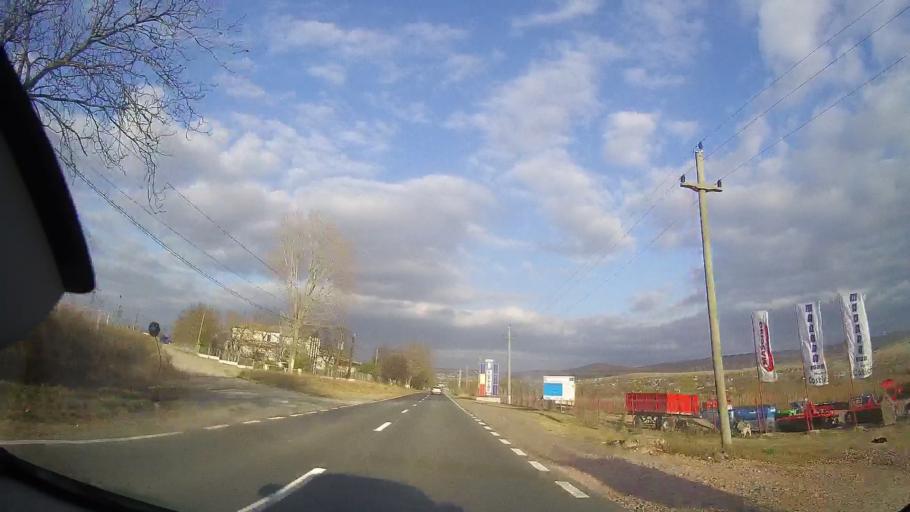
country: RO
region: Tulcea
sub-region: Comuna Topolog
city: Topolog
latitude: 44.8697
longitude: 28.3645
